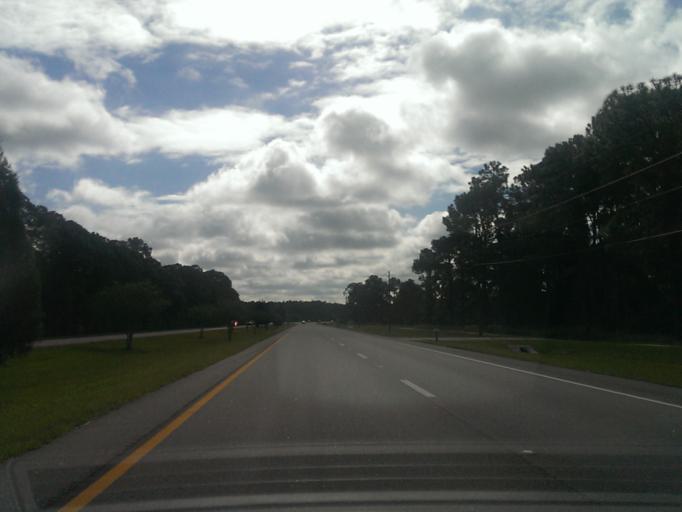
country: US
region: Florida
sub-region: Orange County
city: Bay Hill
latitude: 28.4394
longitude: -81.5396
